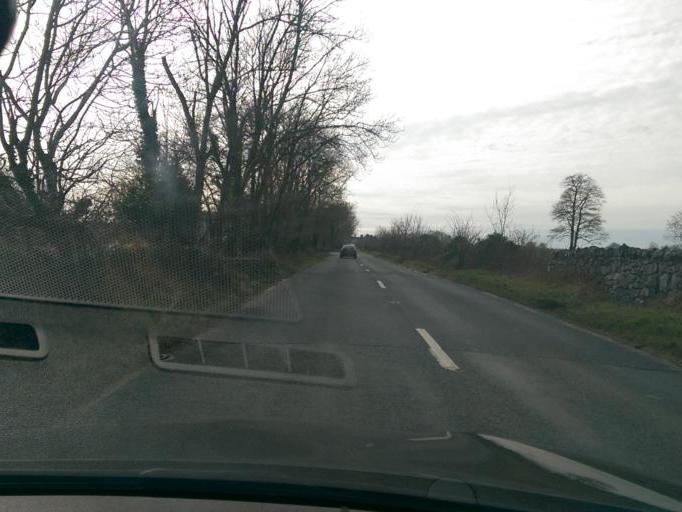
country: IE
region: Connaught
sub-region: County Galway
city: Tuam
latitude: 53.4187
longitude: -8.7938
